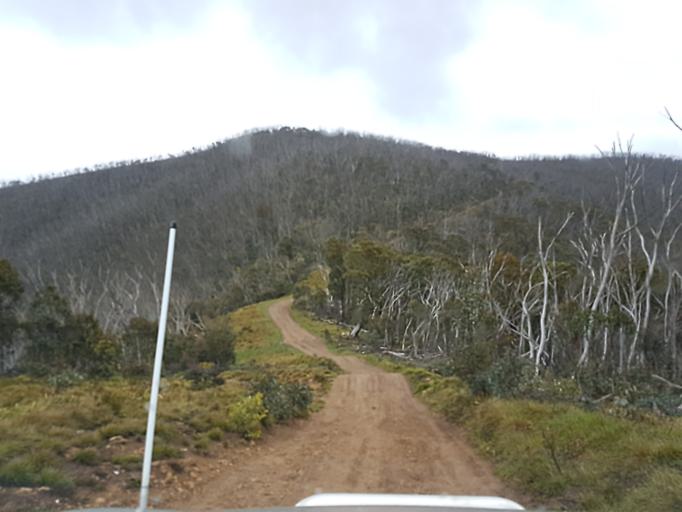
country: AU
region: Victoria
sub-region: Alpine
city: Mount Beauty
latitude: -37.0915
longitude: 147.0970
